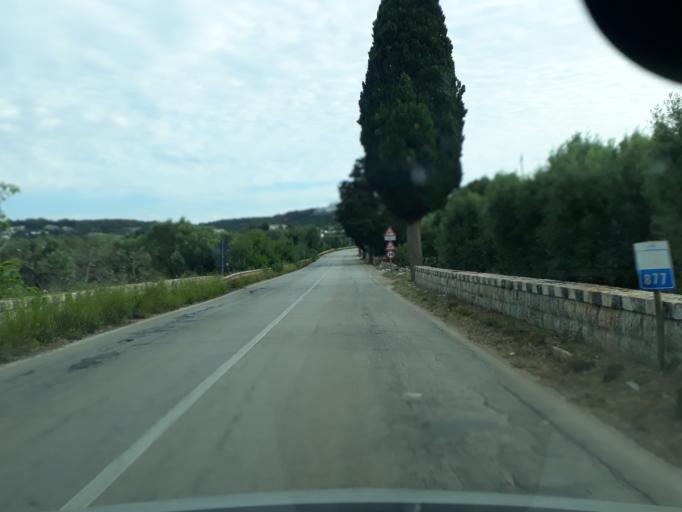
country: IT
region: Apulia
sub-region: Provincia di Brindisi
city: Ostuni
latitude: 40.7444
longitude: 17.5588
